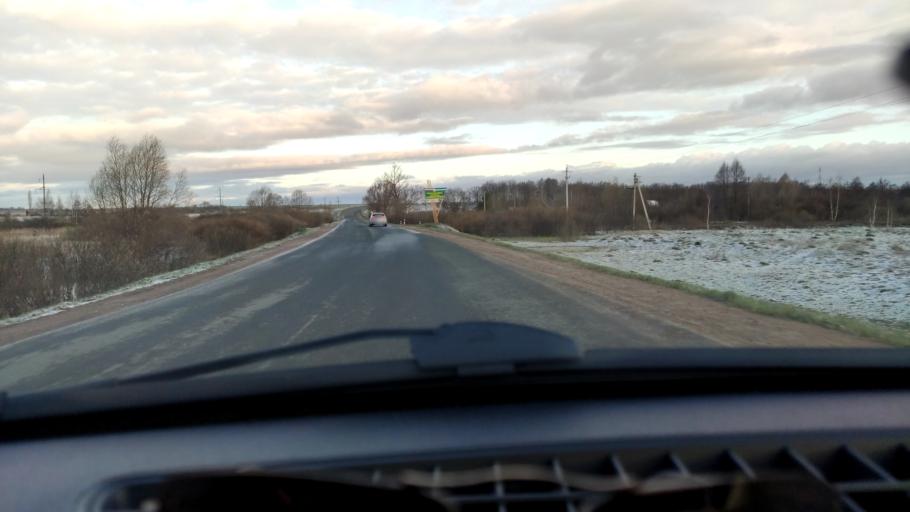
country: RU
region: Bashkortostan
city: Kabakovo
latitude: 54.5081
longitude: 56.1692
